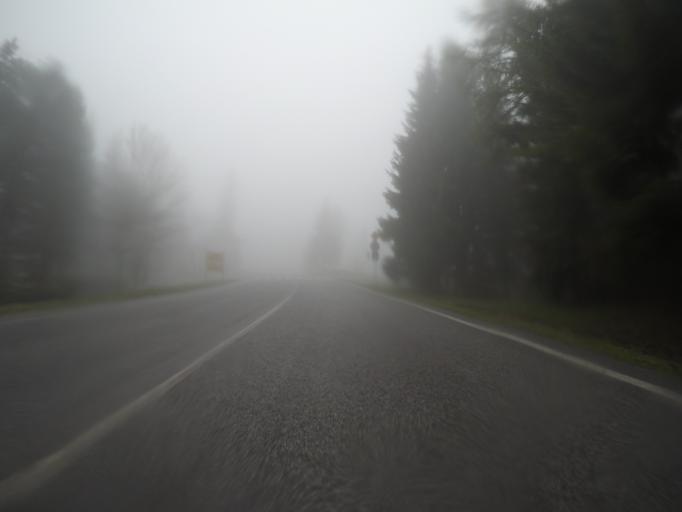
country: SK
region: Presovsky
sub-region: Okres Poprad
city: Strba
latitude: 49.1176
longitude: 20.0681
